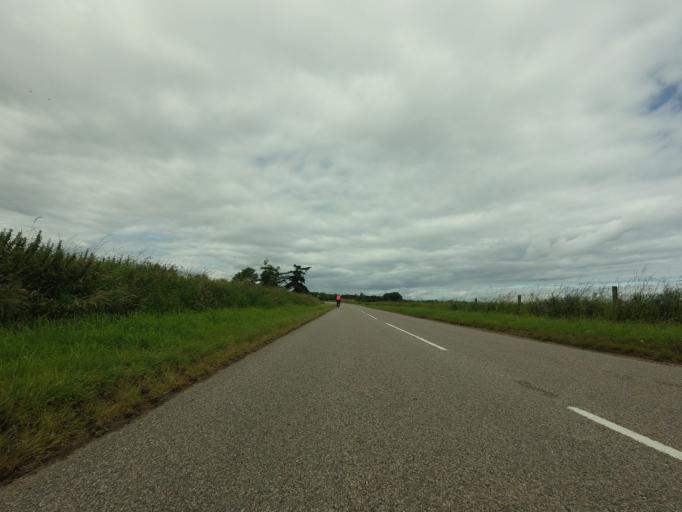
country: GB
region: Scotland
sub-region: Moray
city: Kinloss
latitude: 57.6290
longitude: -3.5502
